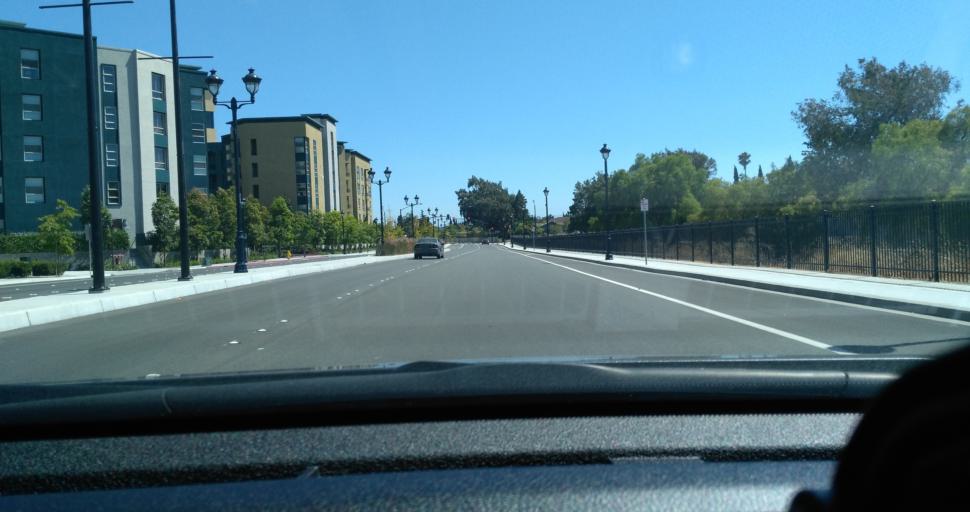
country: US
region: California
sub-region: Santa Clara County
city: Milpitas
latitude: 37.4153
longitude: -121.9050
